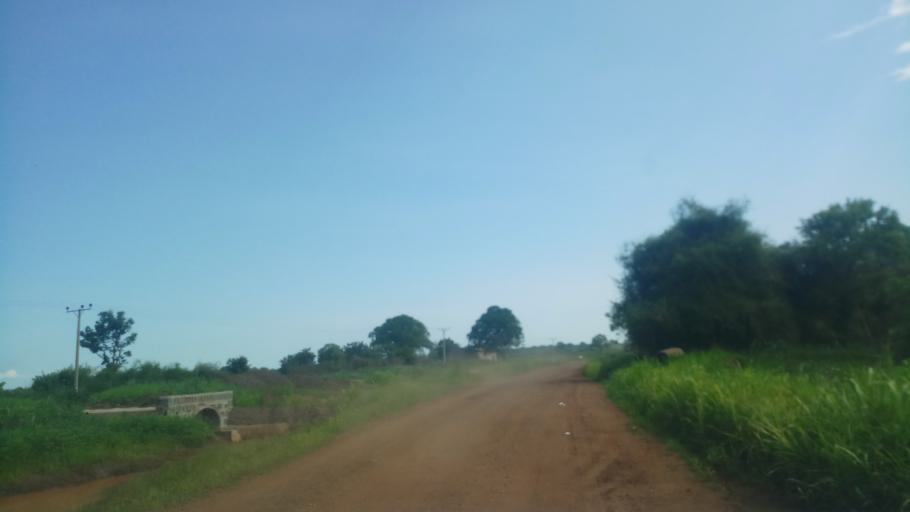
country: ET
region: Gambela
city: Gambela
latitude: 8.1926
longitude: 34.5058
